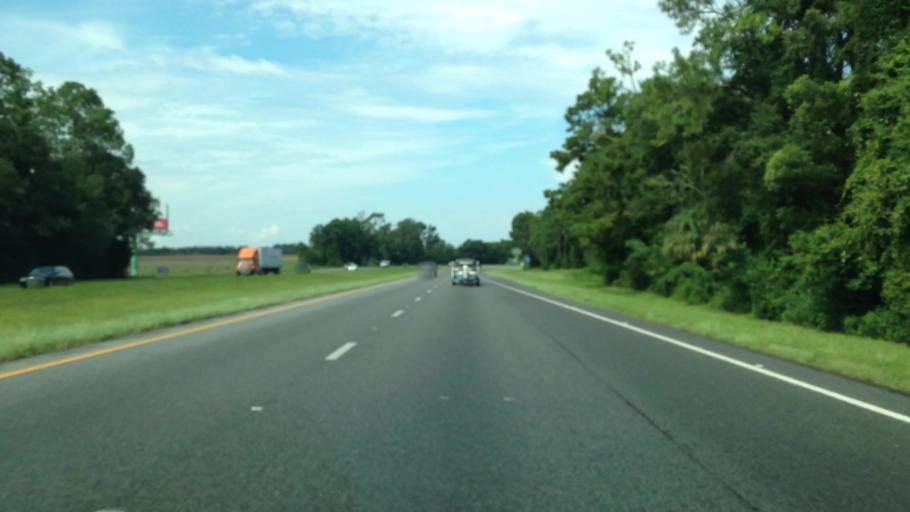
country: US
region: Florida
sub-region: Suwannee County
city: Live Oak
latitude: 30.3400
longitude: -83.0970
